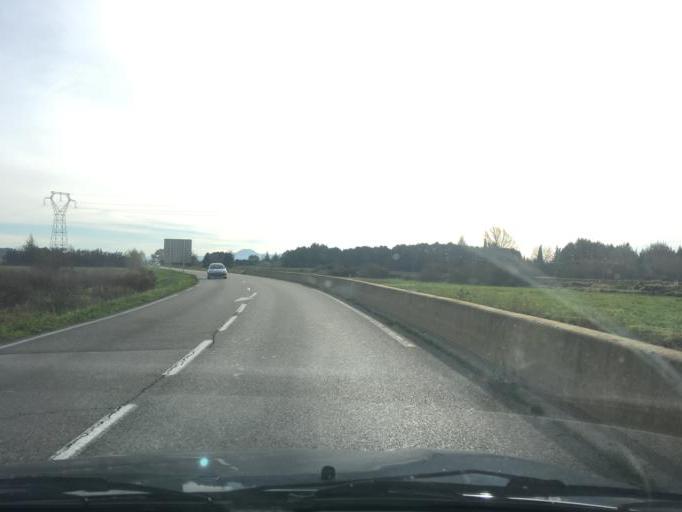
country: FR
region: Provence-Alpes-Cote d'Azur
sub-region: Departement du Vaucluse
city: Villelaure
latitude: 43.7066
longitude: 5.4324
